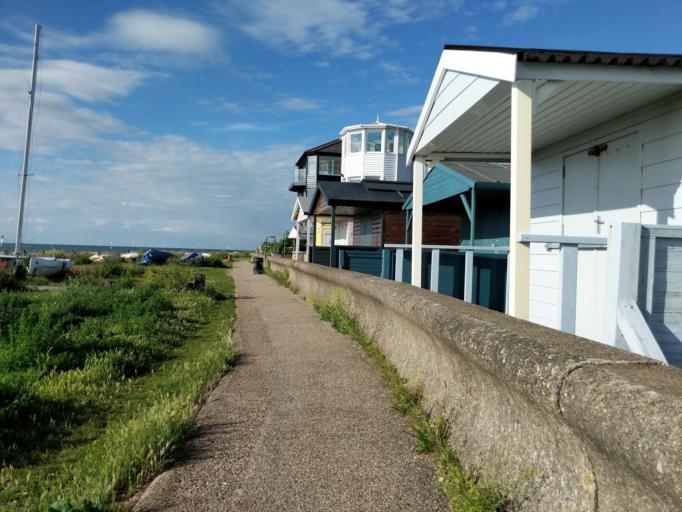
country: GB
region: England
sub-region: Kent
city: Whitstable
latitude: 51.3558
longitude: 1.0167
